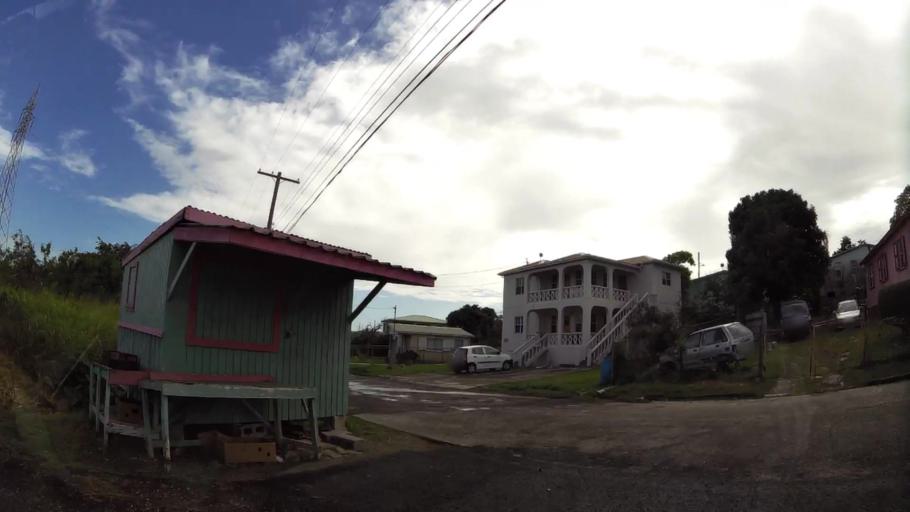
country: AG
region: Saint George
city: Piggotts
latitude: 17.1091
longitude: -61.8133
